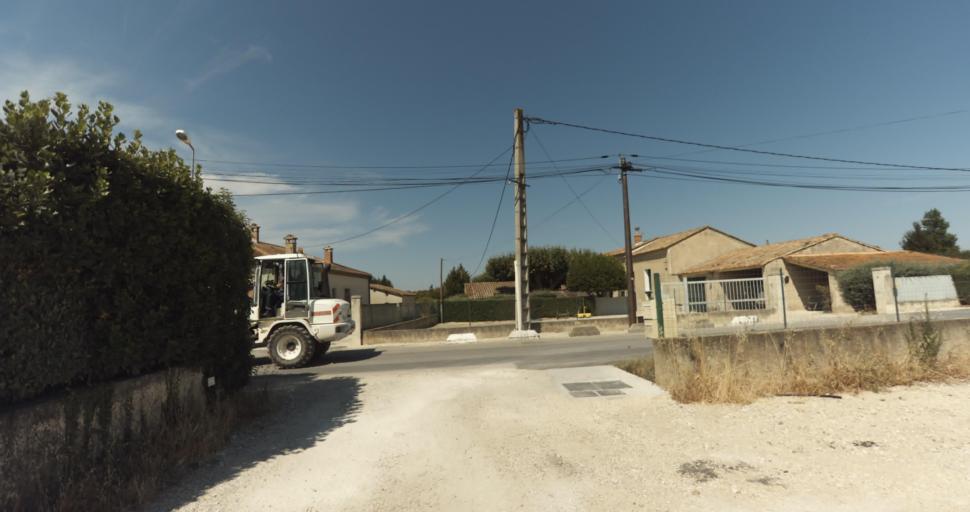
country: FR
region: Provence-Alpes-Cote d'Azur
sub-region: Departement du Vaucluse
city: Monteux
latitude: 44.0250
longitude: 4.9973
